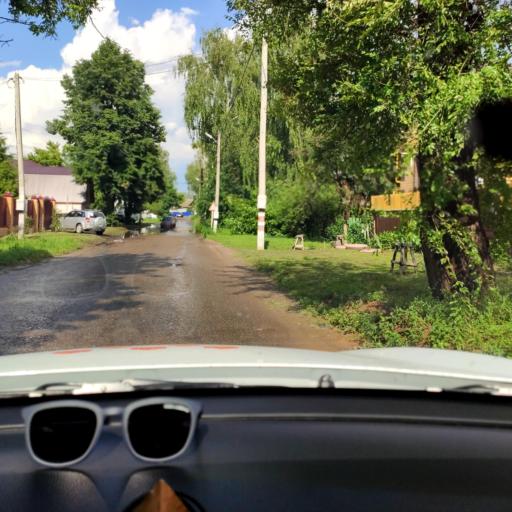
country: RU
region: Tatarstan
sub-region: Zelenodol'skiy Rayon
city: Vasil'yevo
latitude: 55.8331
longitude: 48.7165
